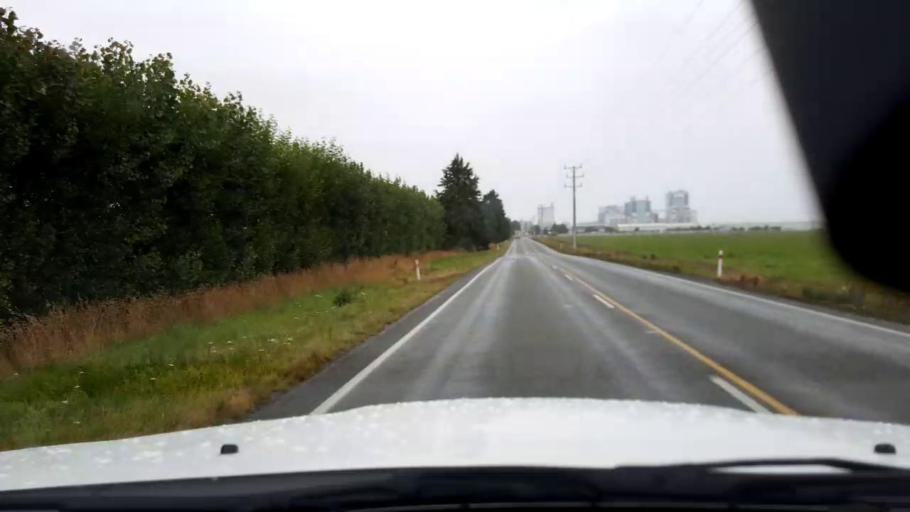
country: NZ
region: Canterbury
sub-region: Timaru District
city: Timaru
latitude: -44.2048
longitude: 171.3745
